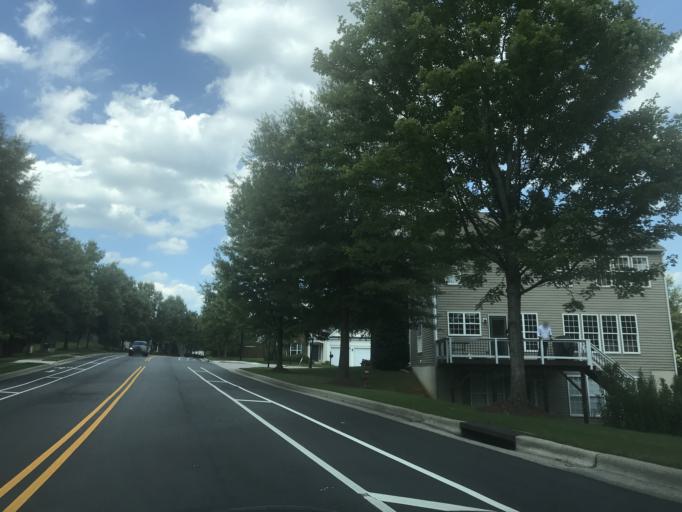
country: US
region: North Carolina
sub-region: Wake County
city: Cary
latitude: 35.8859
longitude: -78.7348
